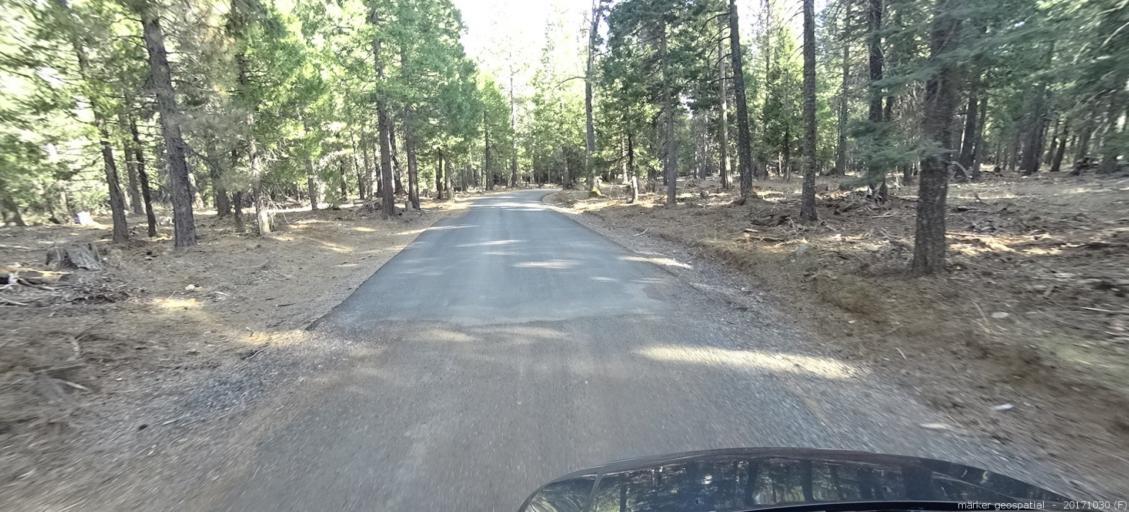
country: US
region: California
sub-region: Shasta County
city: Shingletown
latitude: 40.5588
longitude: -121.7364
